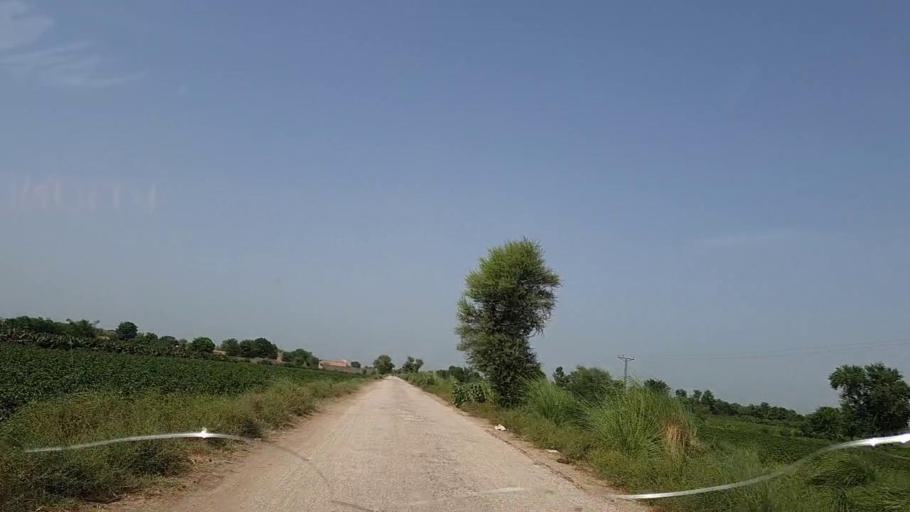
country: PK
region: Sindh
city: Kandiaro
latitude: 27.0315
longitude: 68.1542
